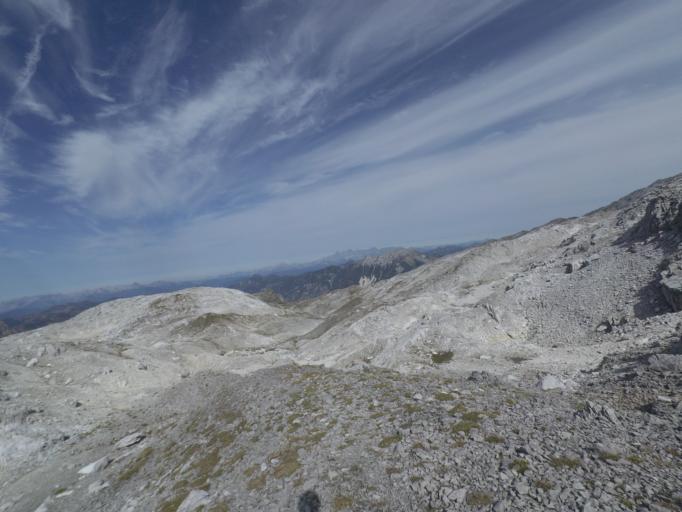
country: AT
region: Salzburg
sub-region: Politischer Bezirk Sankt Johann im Pongau
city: Kleinarl
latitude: 47.2147
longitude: 13.3906
